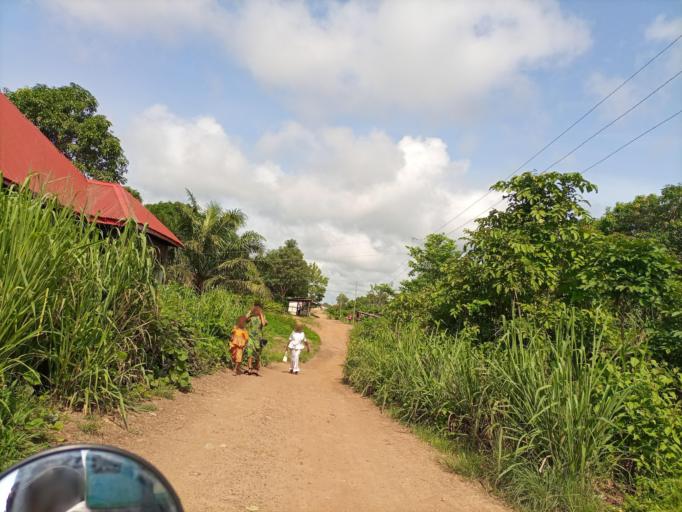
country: SL
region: Southern Province
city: Bo
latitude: 7.9677
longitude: -11.7654
